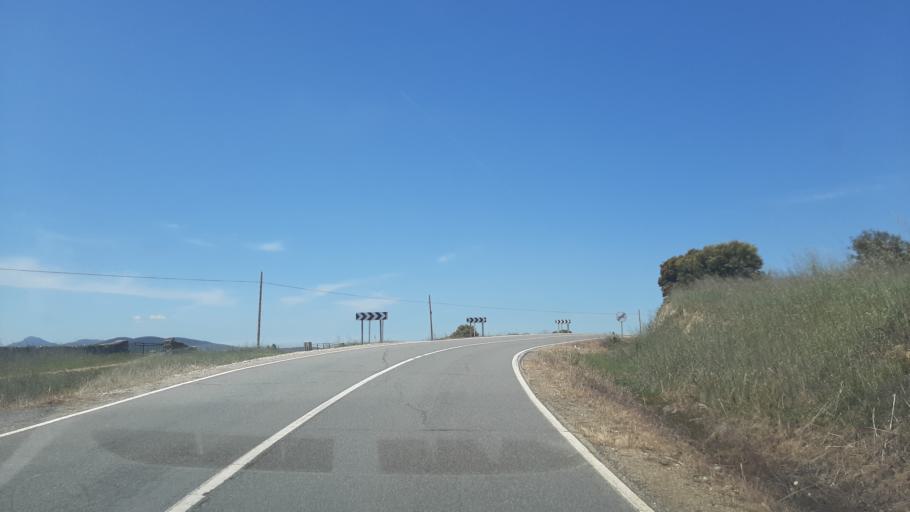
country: ES
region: Castille and Leon
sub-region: Provincia de Salamanca
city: Puente del Congosto
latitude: 40.5325
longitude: -5.5600
